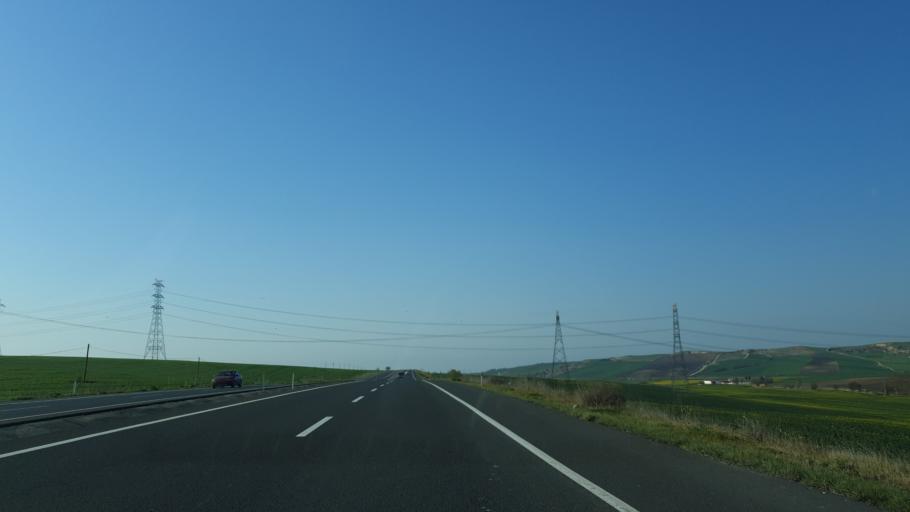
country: TR
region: Tekirdag
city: Corlu
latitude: 41.0750
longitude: 27.7410
